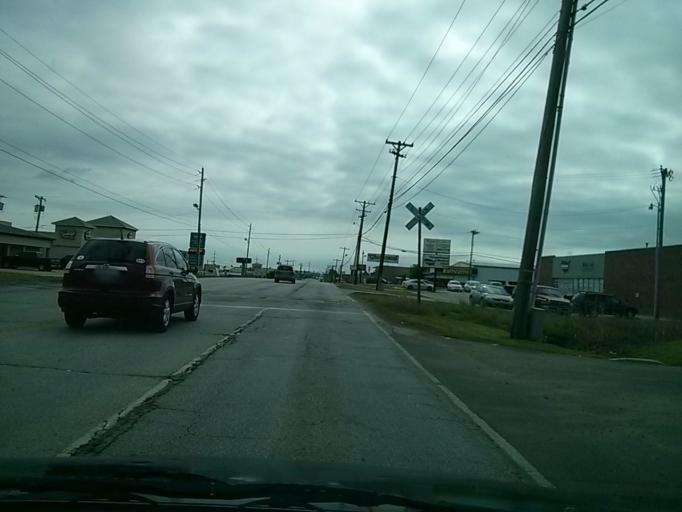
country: US
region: Oklahoma
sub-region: Tulsa County
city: Tulsa
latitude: 36.1044
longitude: -95.9005
